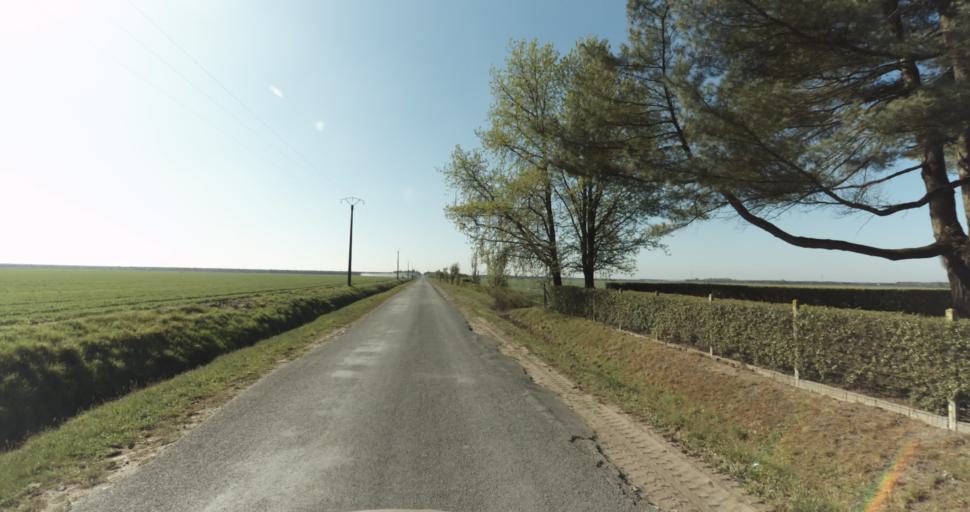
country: FR
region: Aquitaine
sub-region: Departement de la Gironde
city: Marcheprime
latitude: 44.7741
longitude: -0.8582
